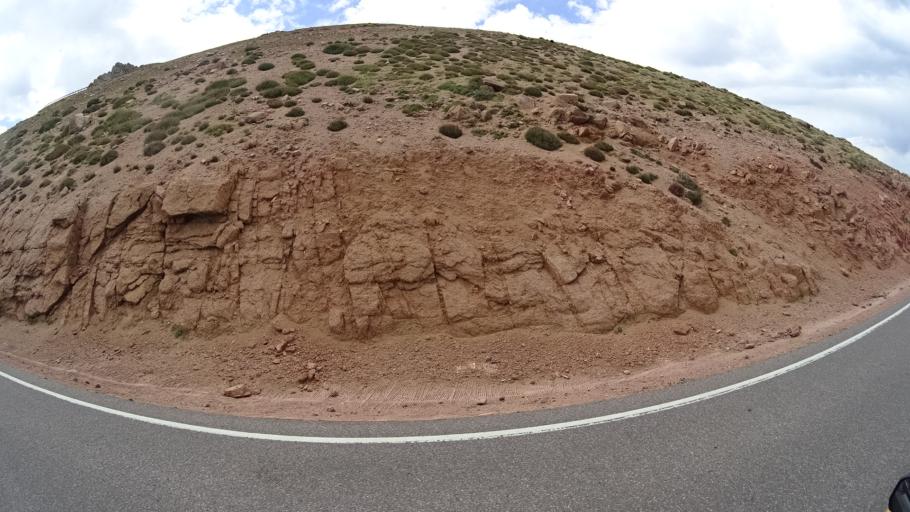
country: US
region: Colorado
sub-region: El Paso County
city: Cascade-Chipita Park
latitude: 38.8680
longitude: -105.0642
